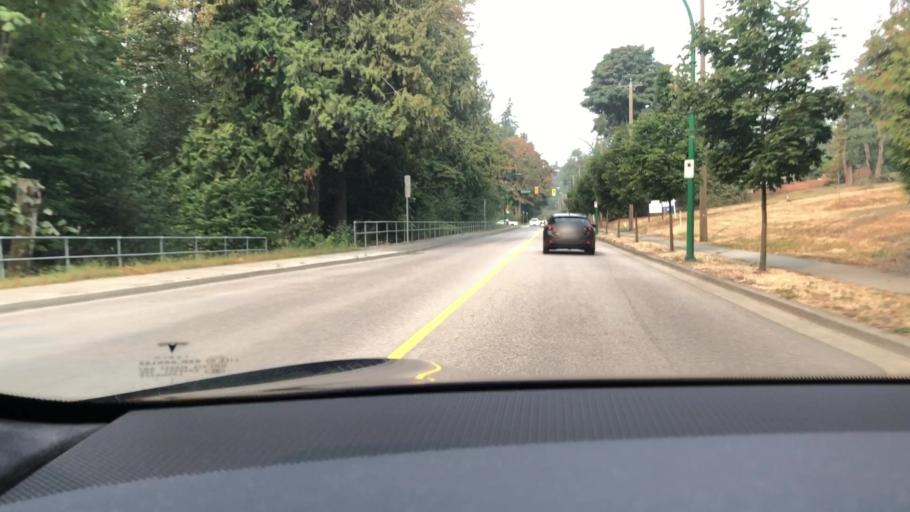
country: CA
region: British Columbia
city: Burnaby
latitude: 49.2092
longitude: -123.0063
